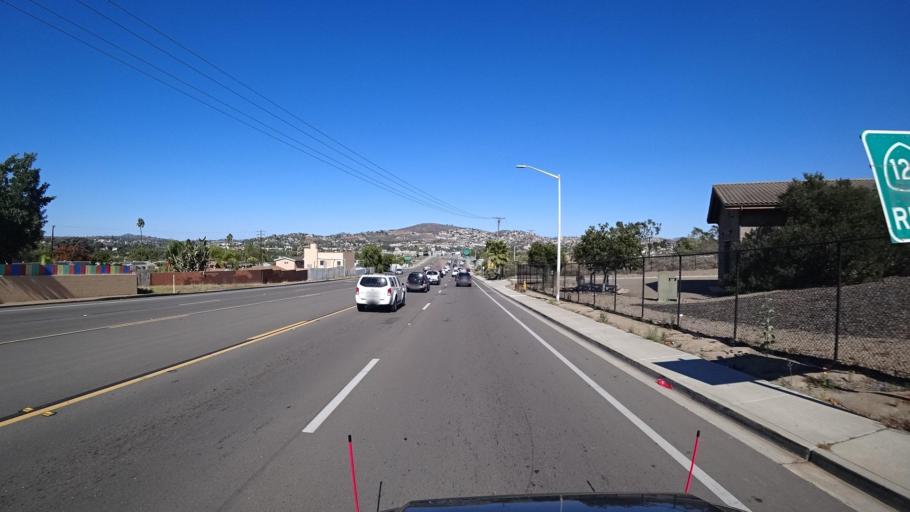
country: US
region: California
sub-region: San Diego County
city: La Presa
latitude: 32.7015
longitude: -117.0136
